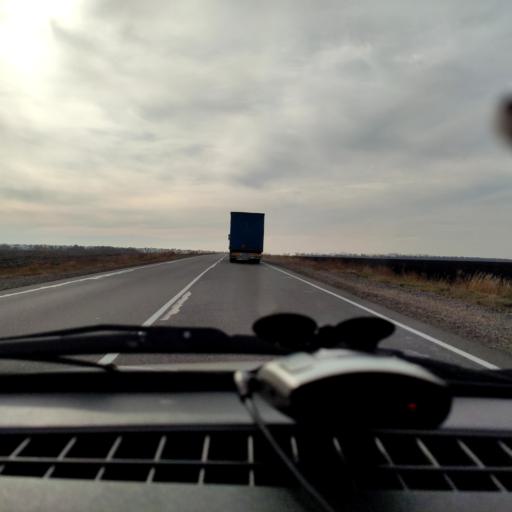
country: RU
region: Voronezj
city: Strelitsa
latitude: 51.4727
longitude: 38.9599
